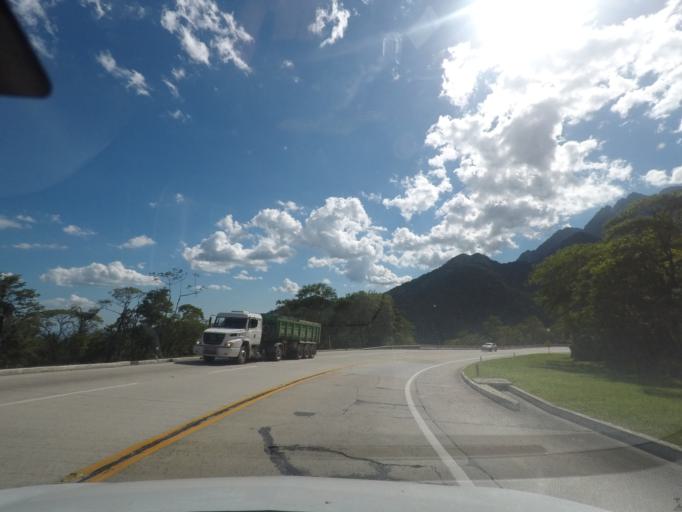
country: BR
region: Rio de Janeiro
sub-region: Guapimirim
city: Guapimirim
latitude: -22.4886
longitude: -42.9978
